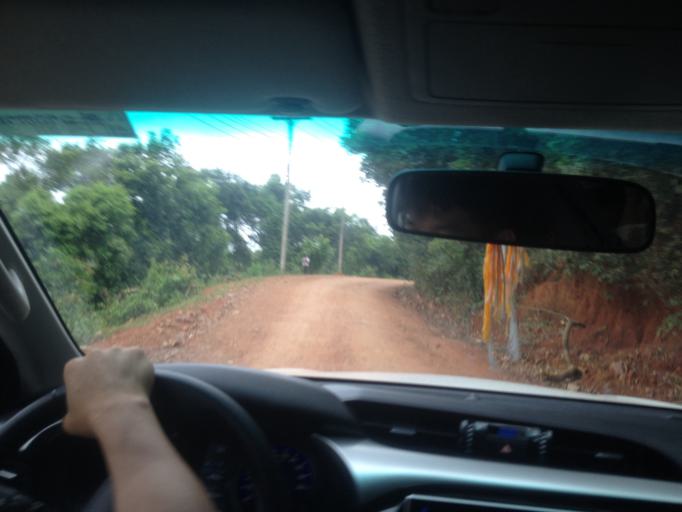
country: TH
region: Nan
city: Chaloem Phra Kiat
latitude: 19.9773
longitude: 101.1358
